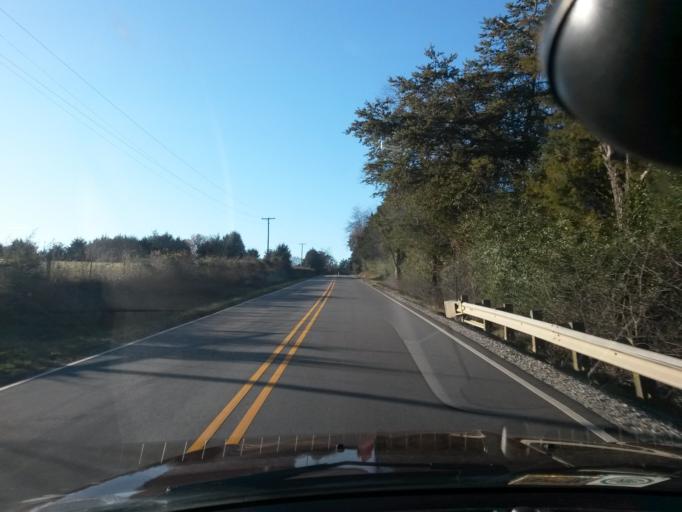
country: US
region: Virginia
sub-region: Amherst County
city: Amherst
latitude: 37.6029
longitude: -79.0681
